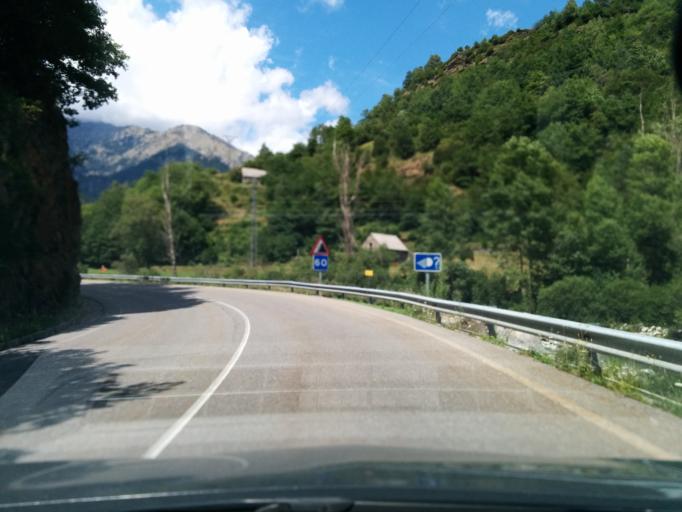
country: ES
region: Aragon
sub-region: Provincia de Huesca
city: Bielsa
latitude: 42.6397
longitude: 0.2149
